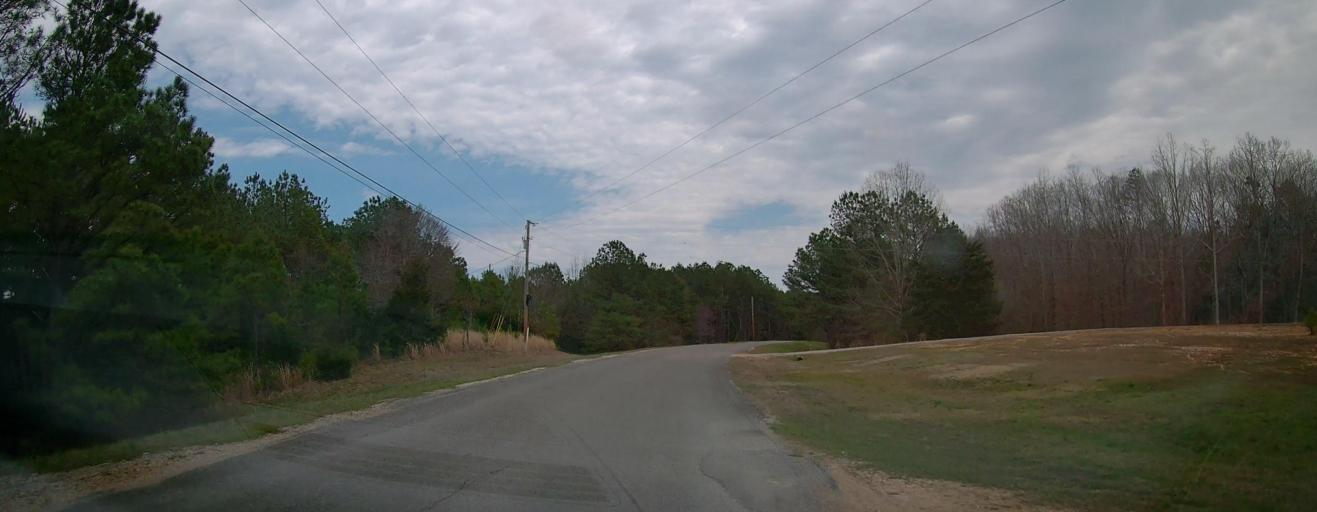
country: US
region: Mississippi
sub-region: Itawamba County
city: Fulton
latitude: 34.2140
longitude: -88.2036
